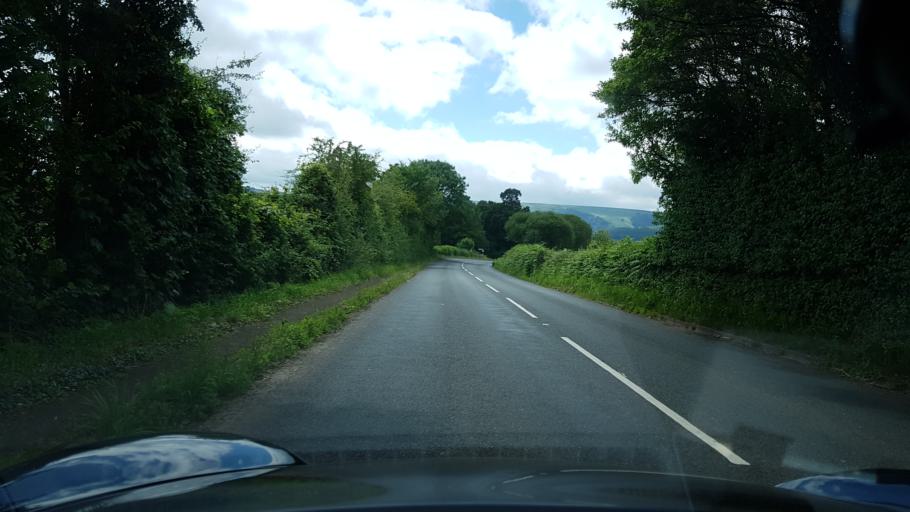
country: GB
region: Wales
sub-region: Monmouthshire
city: Abergavenny
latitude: 51.7866
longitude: -2.9694
